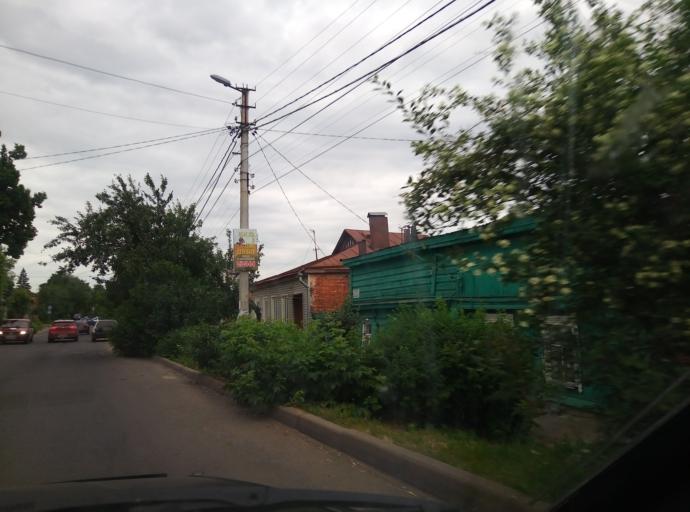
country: RU
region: Kursk
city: Kursk
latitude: 51.7401
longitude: 36.1850
